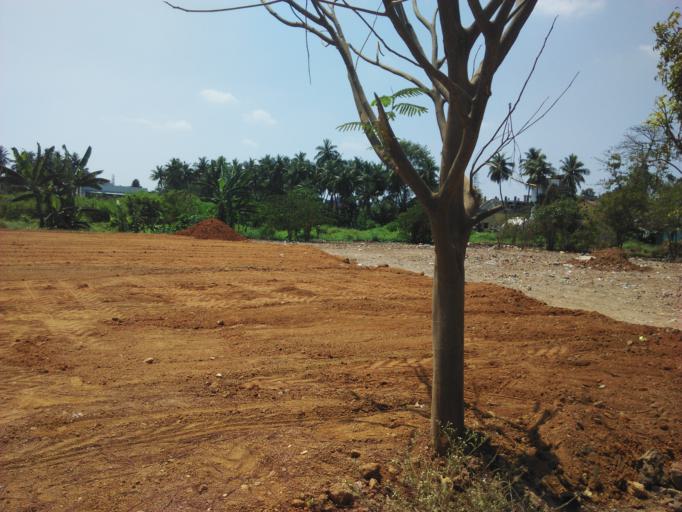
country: IN
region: Tamil Nadu
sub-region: Tiruchchirappalli
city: Tiruchirappalli
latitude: 10.8252
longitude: 78.7026
